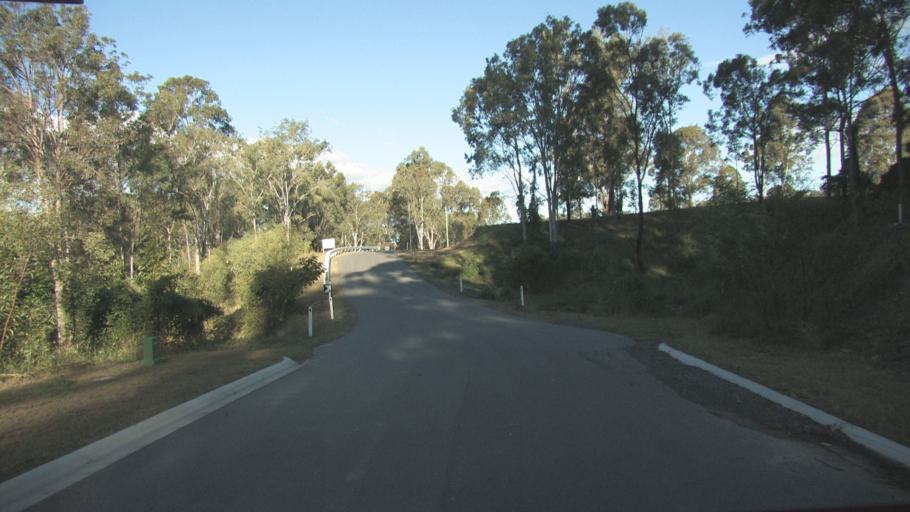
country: AU
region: Queensland
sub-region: Logan
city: Cedar Vale
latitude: -27.9285
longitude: 153.0515
